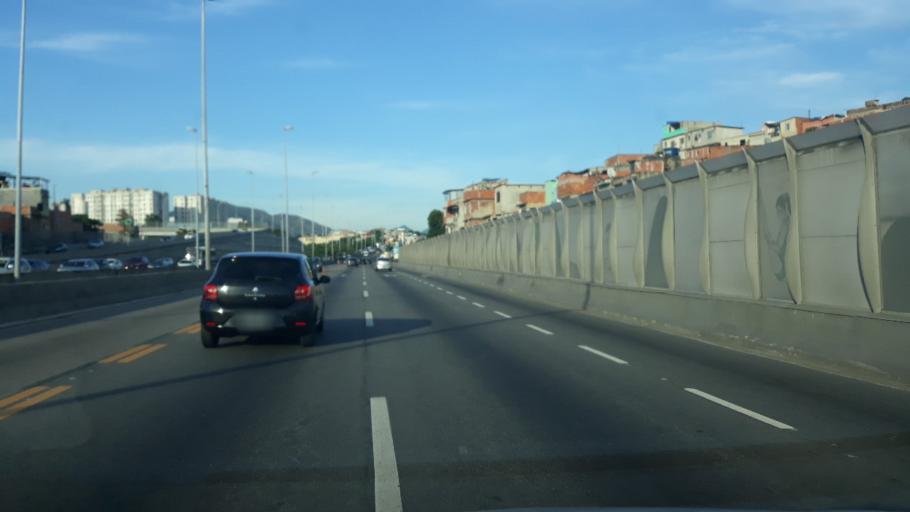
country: BR
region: Rio de Janeiro
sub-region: Rio De Janeiro
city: Rio de Janeiro
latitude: -22.8813
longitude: -43.2823
